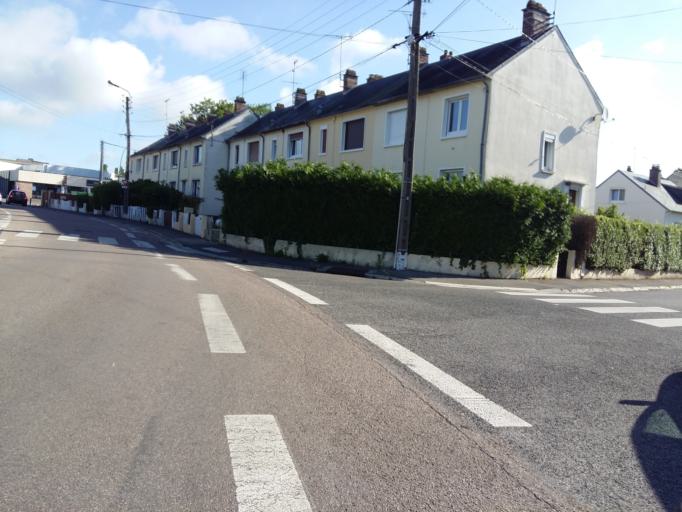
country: FR
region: Picardie
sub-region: Departement de la Somme
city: Rivery
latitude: 49.9084
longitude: 2.3270
